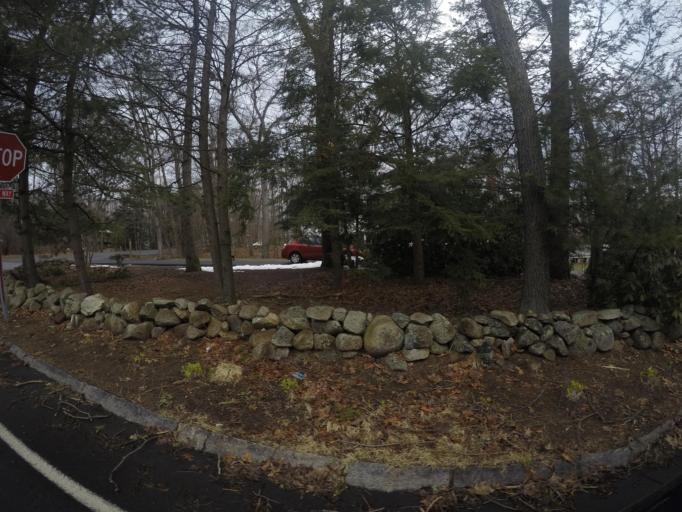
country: US
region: Massachusetts
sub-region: Bristol County
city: Easton
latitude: 42.0489
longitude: -71.1606
